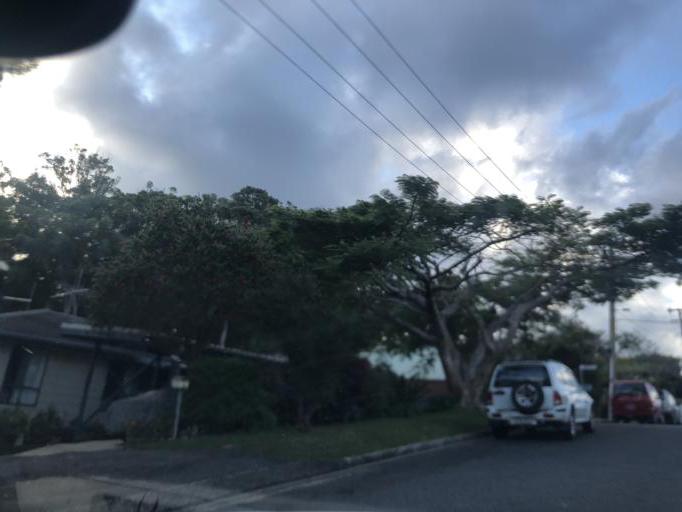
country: AU
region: New South Wales
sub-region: Coffs Harbour
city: Woolgoolga
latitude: -30.0987
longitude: 153.1917
